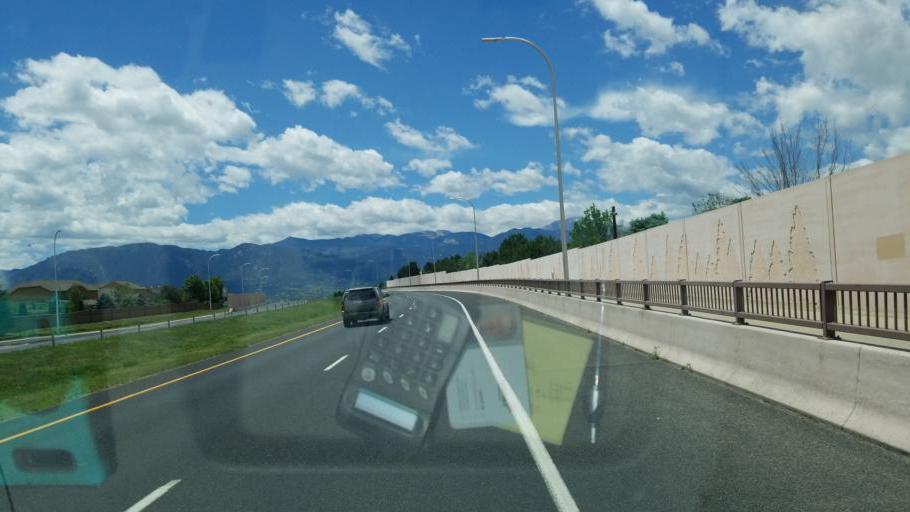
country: US
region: Colorado
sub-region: El Paso County
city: Security-Widefield
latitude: 38.7816
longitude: -104.7296
